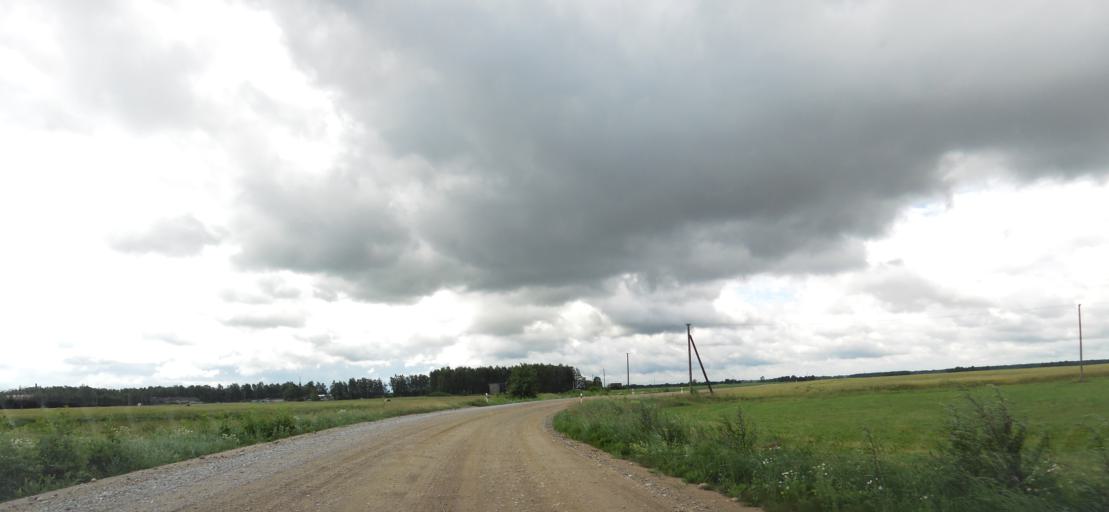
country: LT
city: Vabalninkas
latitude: 55.9872
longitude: 24.7394
